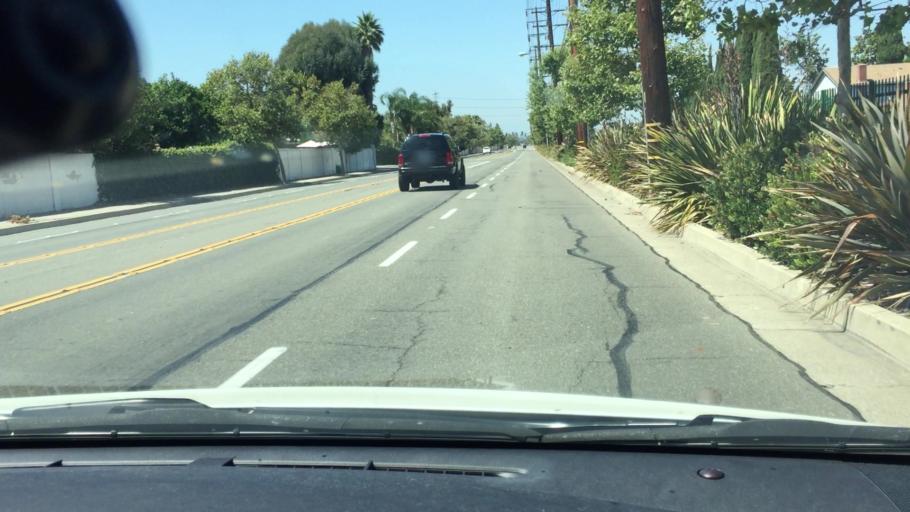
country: US
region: California
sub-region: Orange County
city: Santa Ana
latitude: 33.7019
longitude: -117.8769
